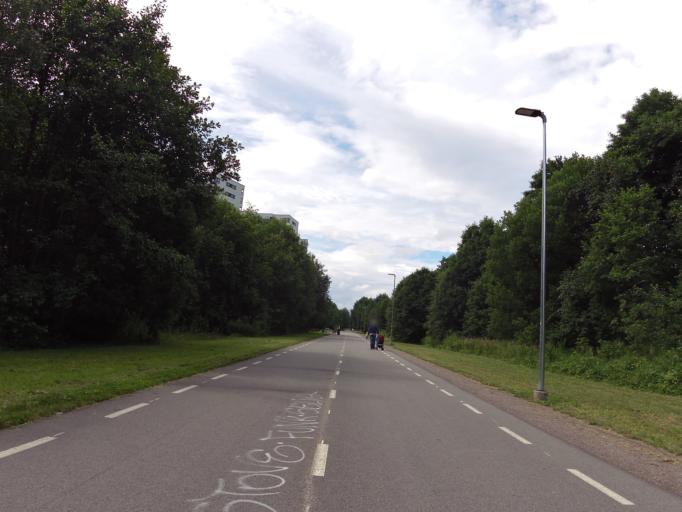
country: EE
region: Harju
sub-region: Saue vald
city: Laagri
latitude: 59.4095
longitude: 24.6537
